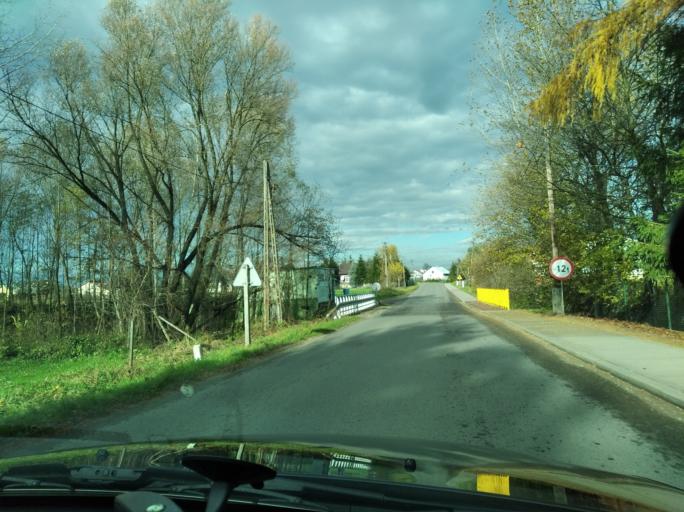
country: PL
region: Subcarpathian Voivodeship
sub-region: Powiat debicki
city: Brzeznica
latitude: 50.0836
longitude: 21.5212
